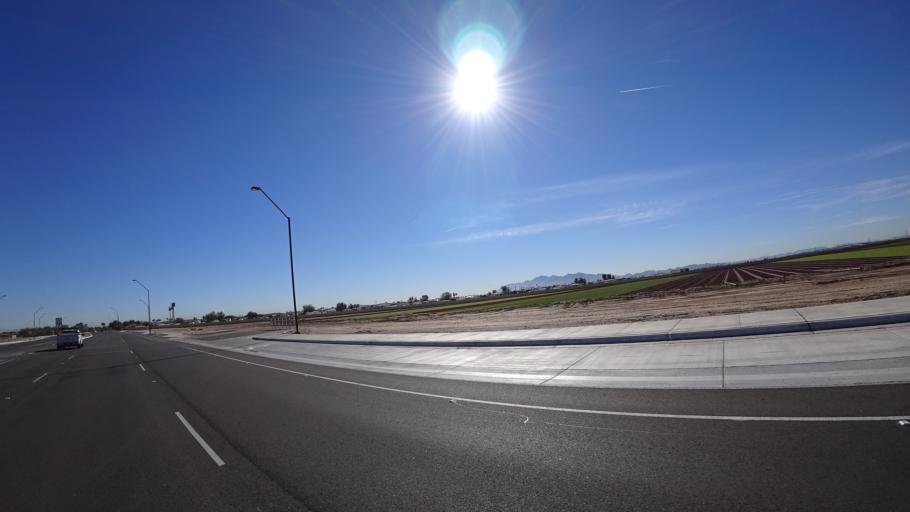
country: US
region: Arizona
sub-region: Maricopa County
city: Litchfield Park
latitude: 33.4936
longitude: -112.4169
